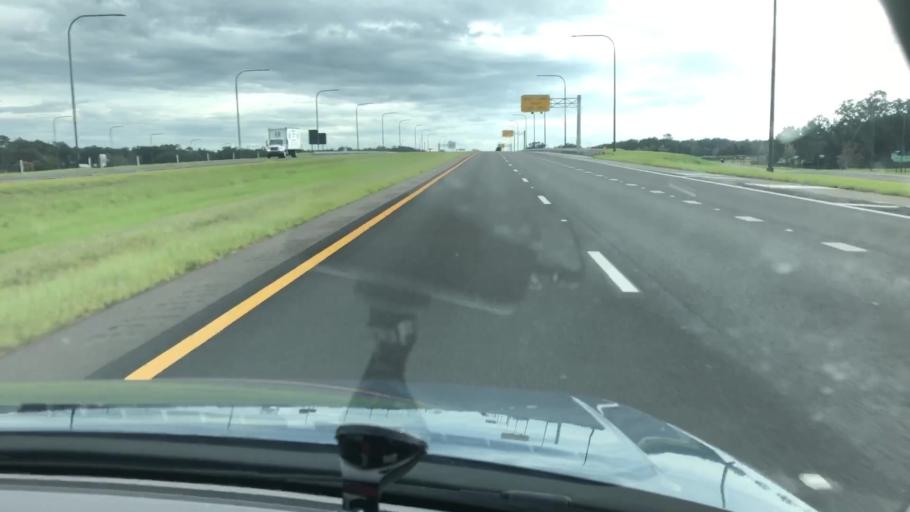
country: US
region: Florida
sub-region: Orange County
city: Zellwood
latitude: 28.7602
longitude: -81.5671
